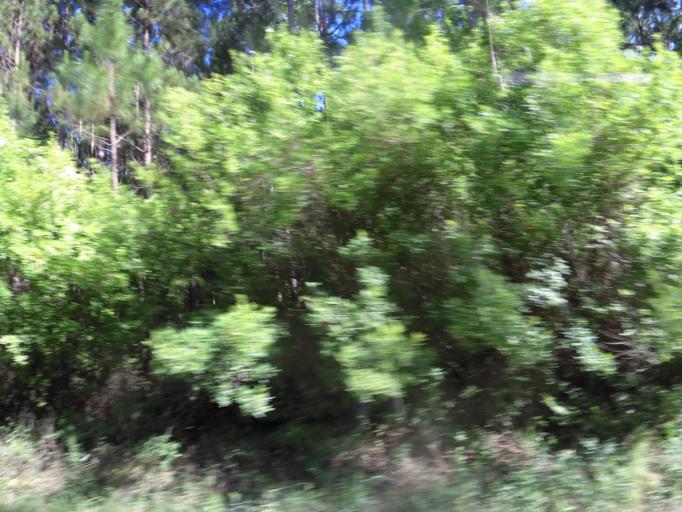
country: US
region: Florida
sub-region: Nassau County
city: Callahan
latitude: 30.5726
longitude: -81.7776
